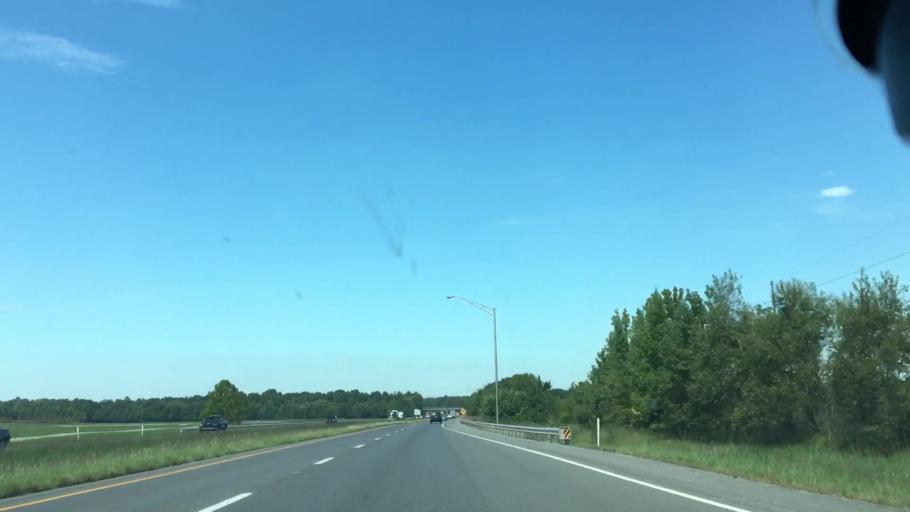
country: US
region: Kentucky
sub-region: Hopkins County
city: Madisonville
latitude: 37.2997
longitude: -87.4641
